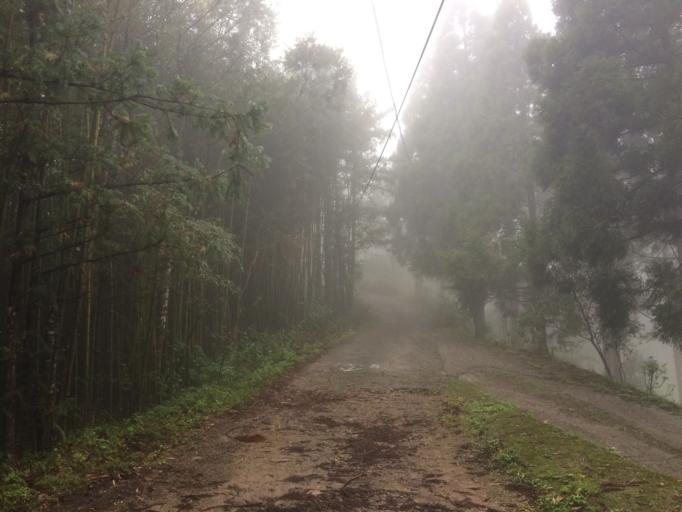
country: TW
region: Taiwan
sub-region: Hsinchu
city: Hsinchu
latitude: 24.5775
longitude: 121.0959
